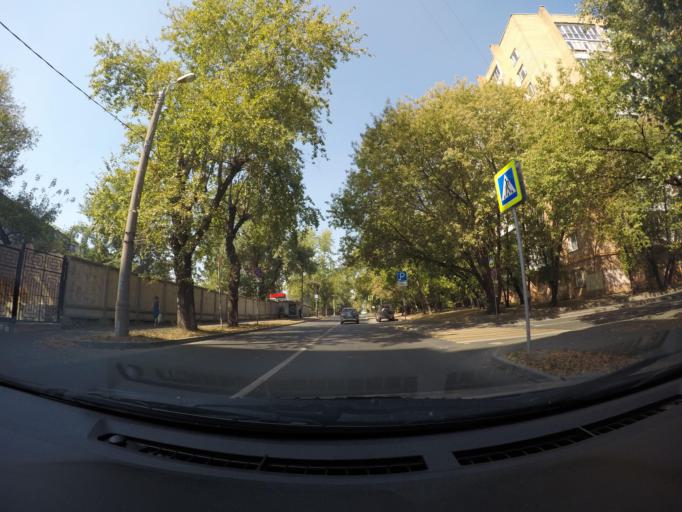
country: RU
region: Moscow
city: Sokol'niki
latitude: 55.7877
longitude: 37.6709
